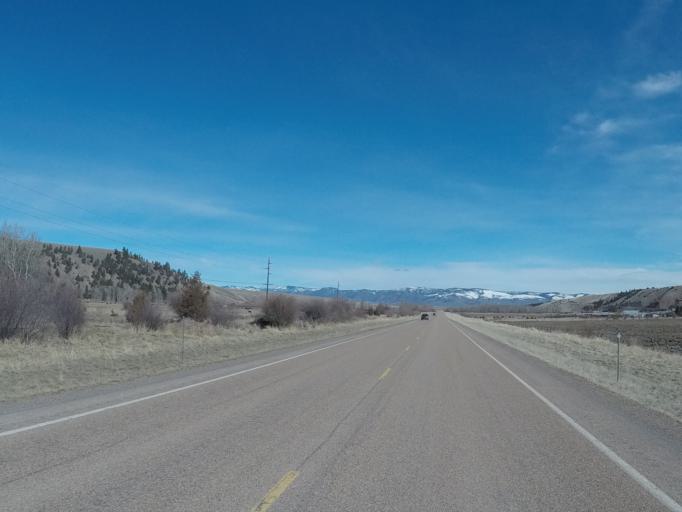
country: US
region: Montana
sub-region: Granite County
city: Philipsburg
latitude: 46.5177
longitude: -113.2269
